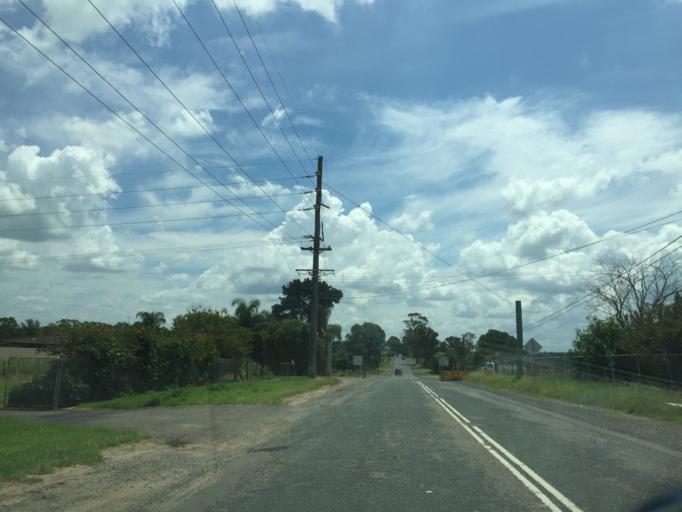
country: AU
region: New South Wales
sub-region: Blacktown
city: Riverstone
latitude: -33.7042
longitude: 150.8869
